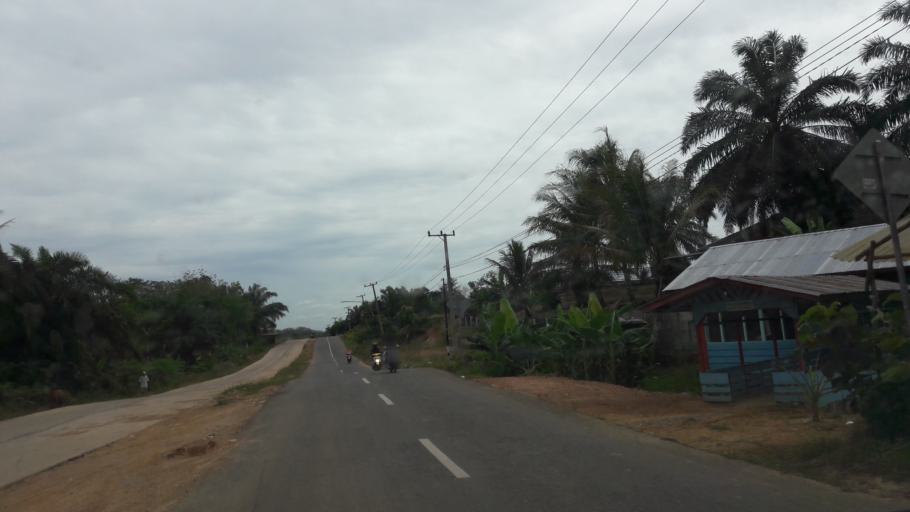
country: ID
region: South Sumatra
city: Gunungmegang Dalam
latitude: -3.2537
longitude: 103.8282
